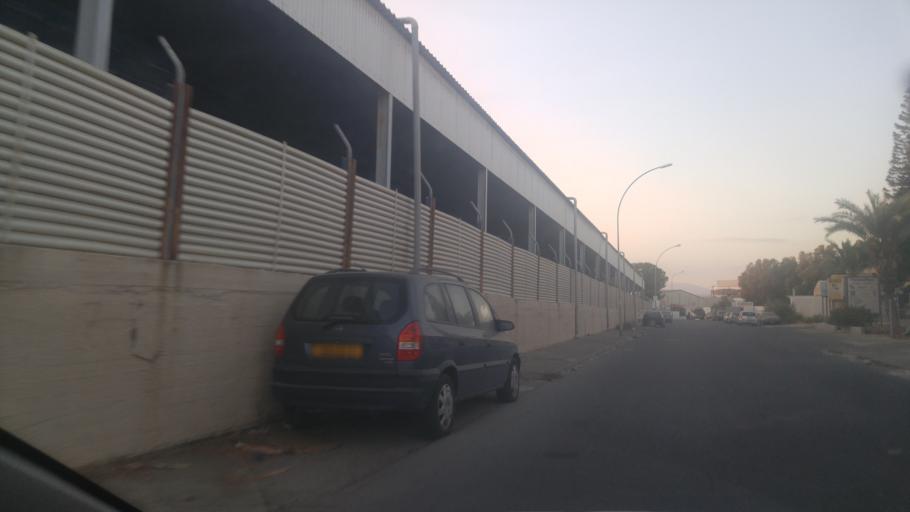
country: CY
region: Limassol
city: Ypsonas
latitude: 34.6666
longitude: 32.9944
